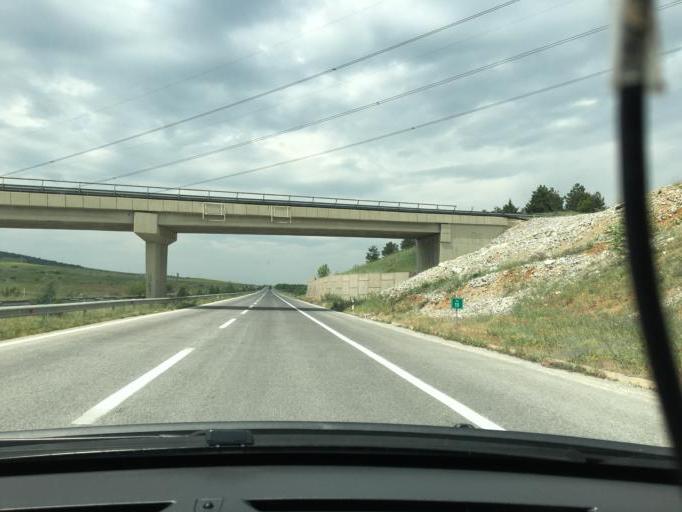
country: MK
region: Negotino
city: Negotino
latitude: 41.4608
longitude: 22.1358
